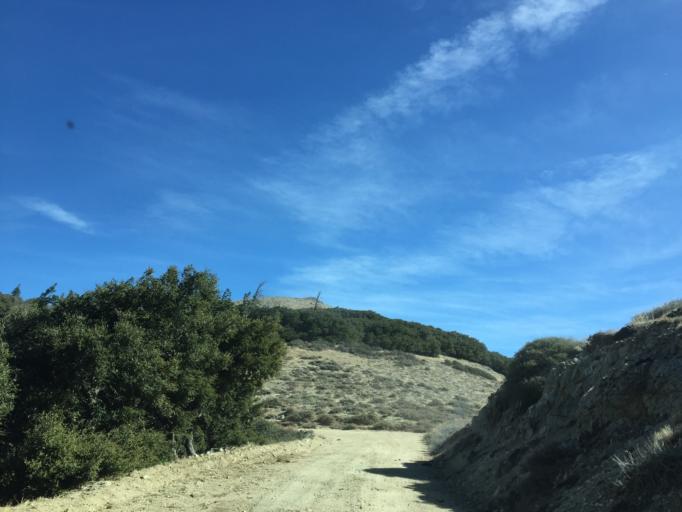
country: US
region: California
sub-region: Kern County
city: Stallion Springs
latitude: 34.9232
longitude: -118.6506
